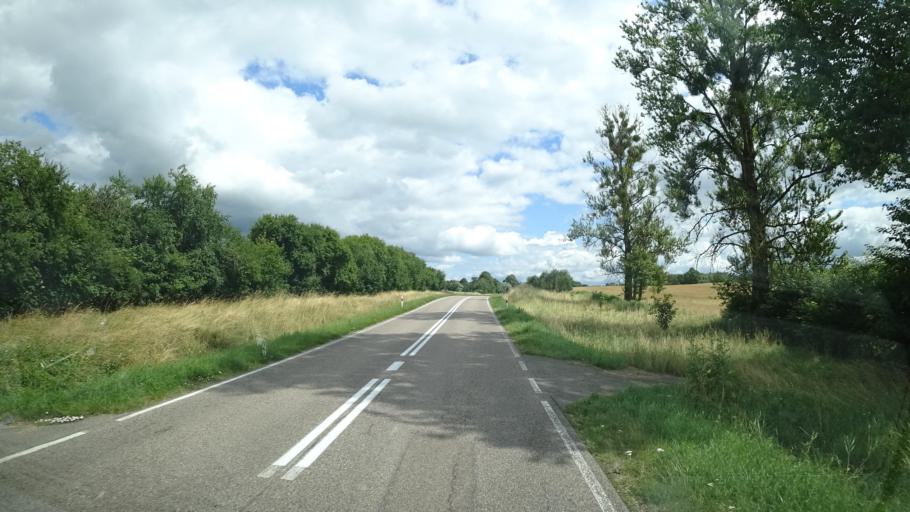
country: PL
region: Warmian-Masurian Voivodeship
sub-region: Powiat goldapski
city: Banie Mazurskie
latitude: 54.2108
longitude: 22.1791
